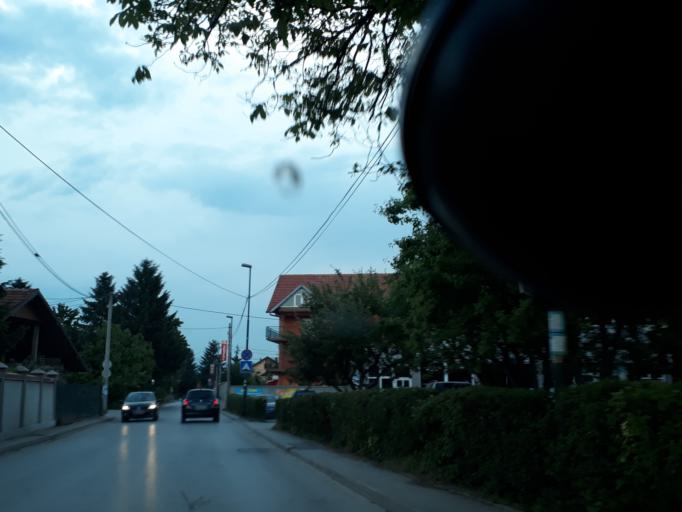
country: BA
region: Federation of Bosnia and Herzegovina
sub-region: Kanton Sarajevo
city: Sarajevo
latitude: 43.8320
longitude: 18.3235
